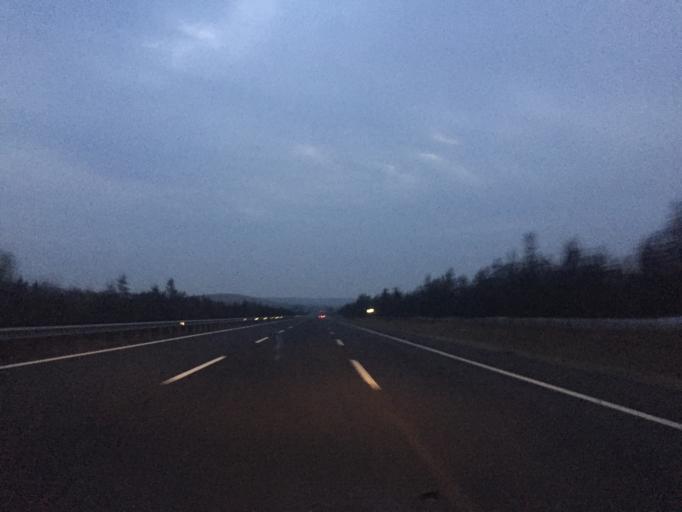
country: TR
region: Sanliurfa
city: Camlidere
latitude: 37.1993
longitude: 38.9384
